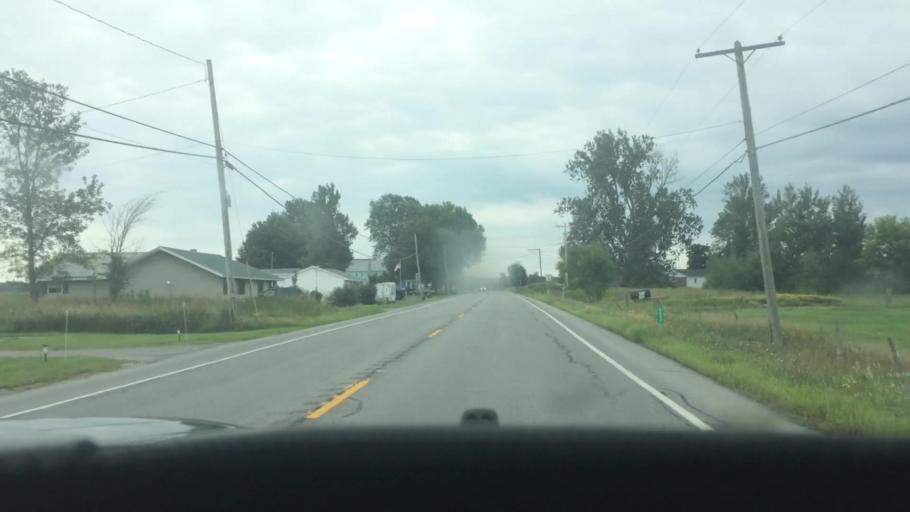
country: US
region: New York
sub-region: St. Lawrence County
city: Ogdensburg
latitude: 44.6689
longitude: -75.4704
